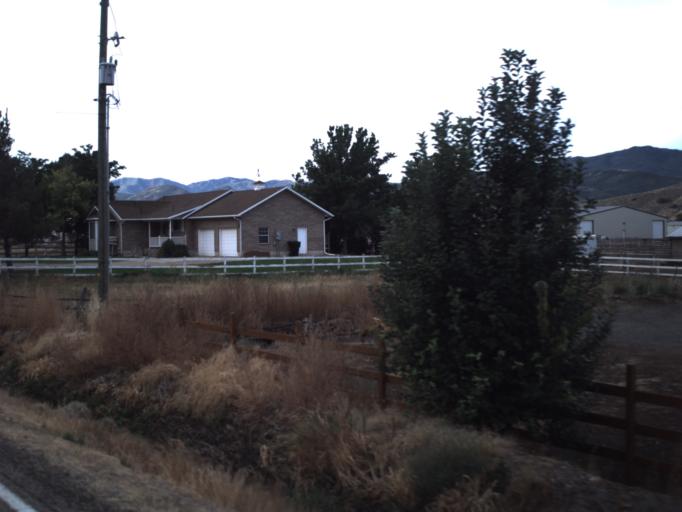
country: US
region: Utah
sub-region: Morgan County
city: Morgan
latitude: 41.0228
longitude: -111.6750
